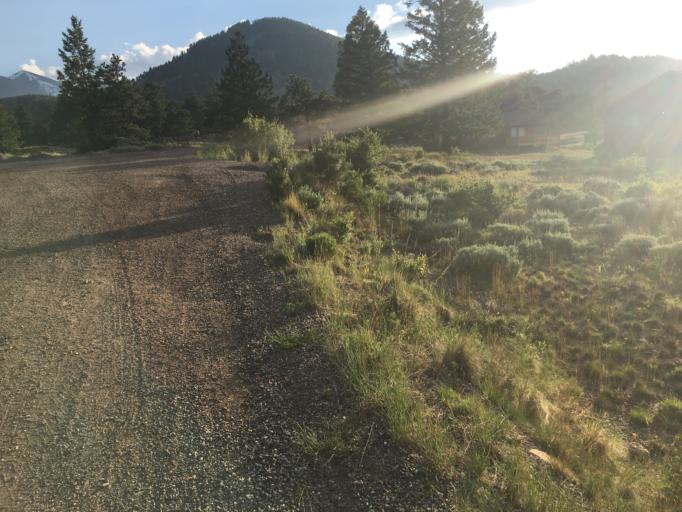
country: US
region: Colorado
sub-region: Larimer County
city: Estes Park
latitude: 40.3358
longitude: -105.5692
